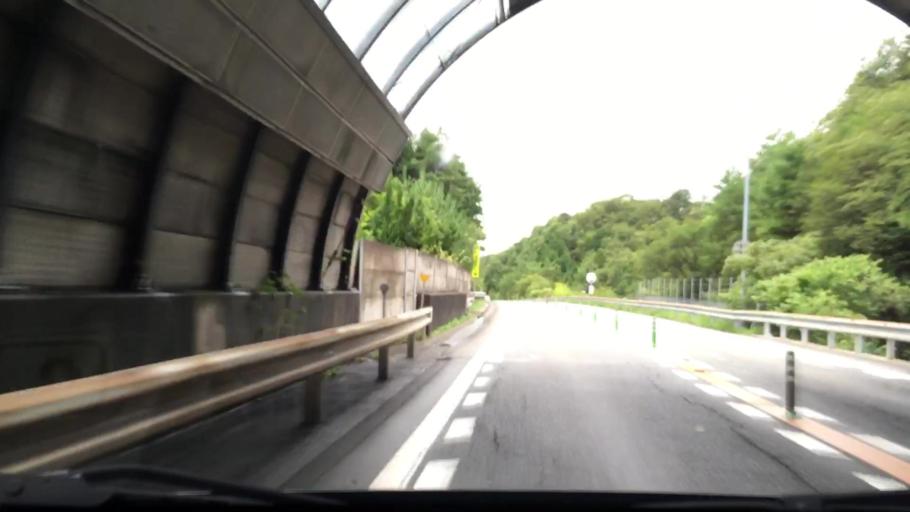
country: JP
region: Hyogo
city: Nishiwaki
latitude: 35.0766
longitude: 134.7710
